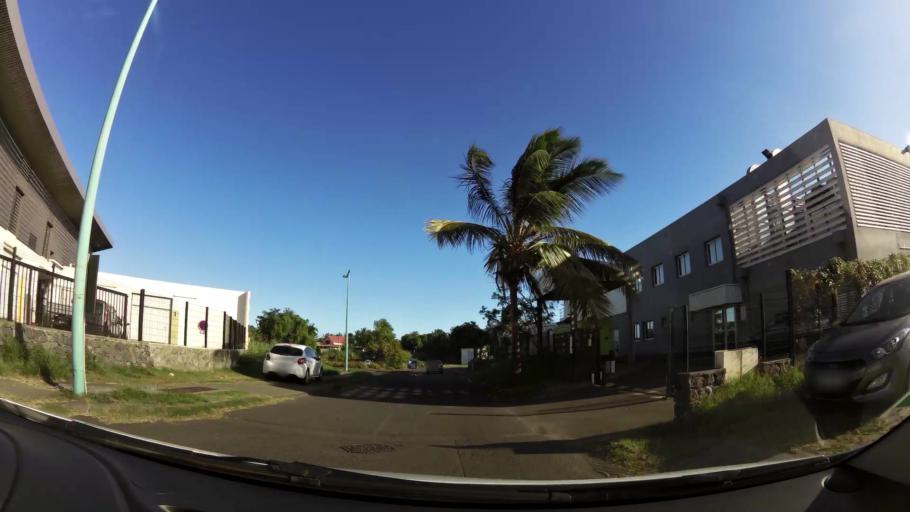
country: RE
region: Reunion
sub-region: Reunion
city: Saint-Louis
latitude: -21.2786
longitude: 55.3766
